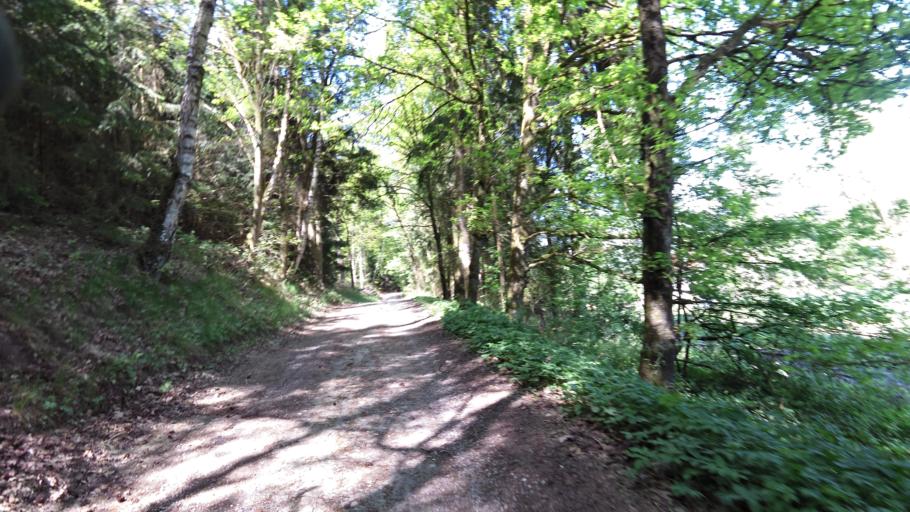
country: DE
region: Bavaria
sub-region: Lower Bavaria
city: Weihmichl
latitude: 48.5751
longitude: 12.0652
